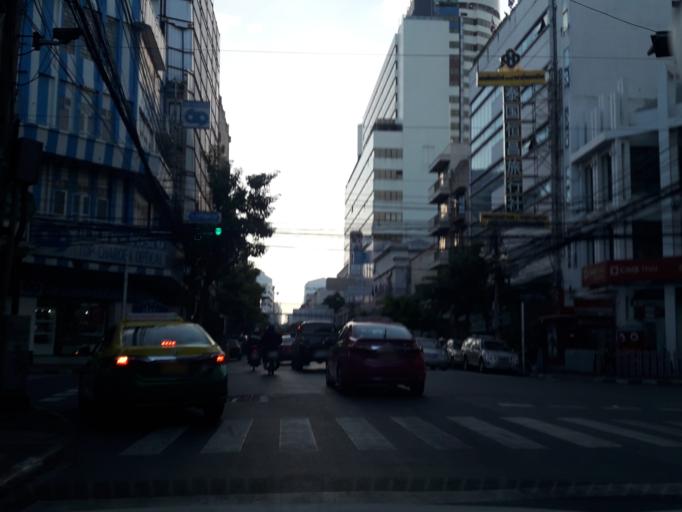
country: TH
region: Bangkok
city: Bangkok
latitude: 13.7440
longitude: 100.5081
